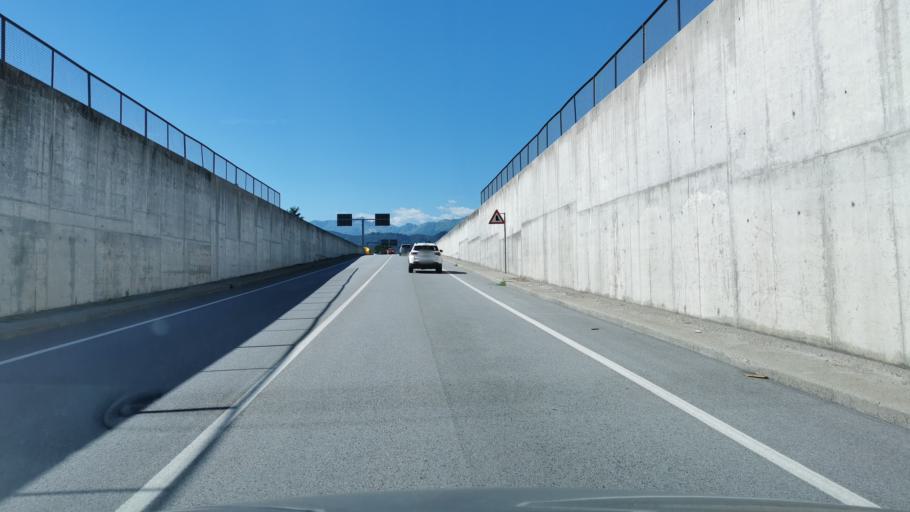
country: IT
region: Piedmont
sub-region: Provincia di Cuneo
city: Cuneo
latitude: 44.3674
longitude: 7.5519
